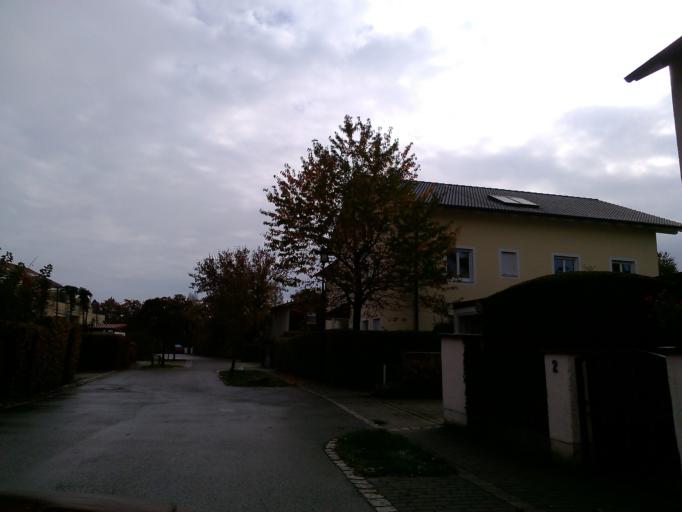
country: DE
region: Bavaria
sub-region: Upper Bavaria
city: Gauting
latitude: 48.0660
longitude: 11.3701
